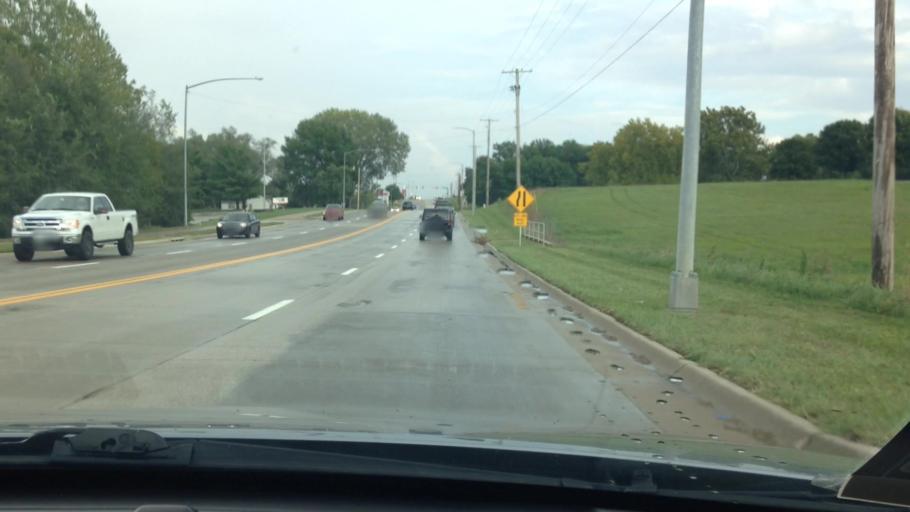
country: US
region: Kansas
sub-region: Leavenworth County
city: Lansing
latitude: 39.2667
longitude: -94.9253
